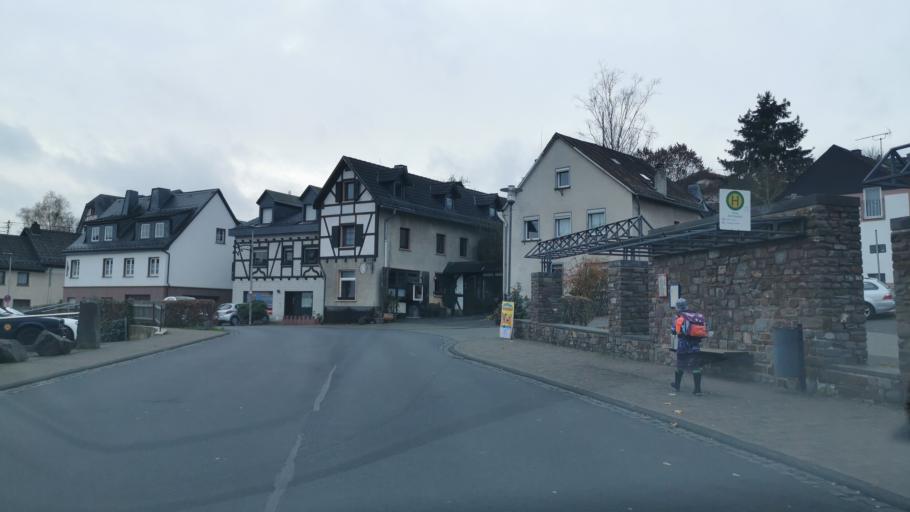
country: DE
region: Rheinland-Pfalz
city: Ulmen
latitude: 50.2093
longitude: 6.9787
